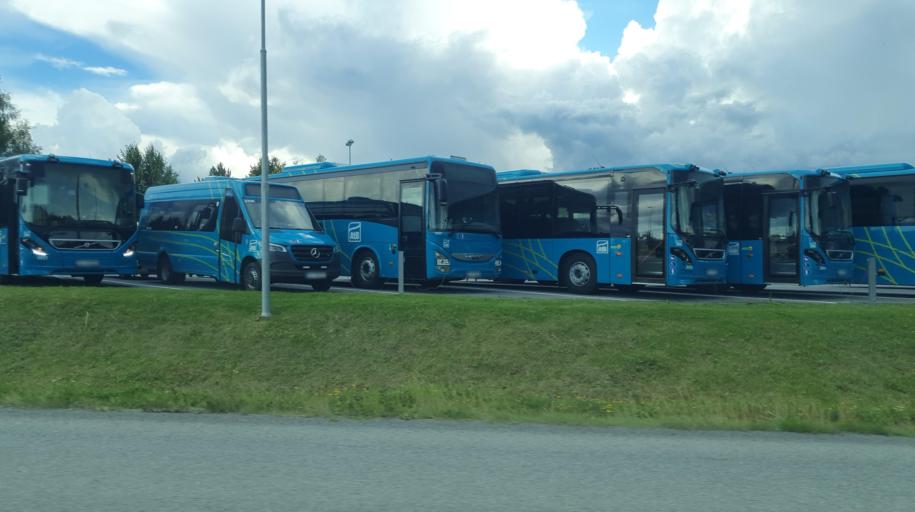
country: NO
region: Nord-Trondelag
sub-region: Levanger
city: Levanger
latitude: 63.7509
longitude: 11.3170
